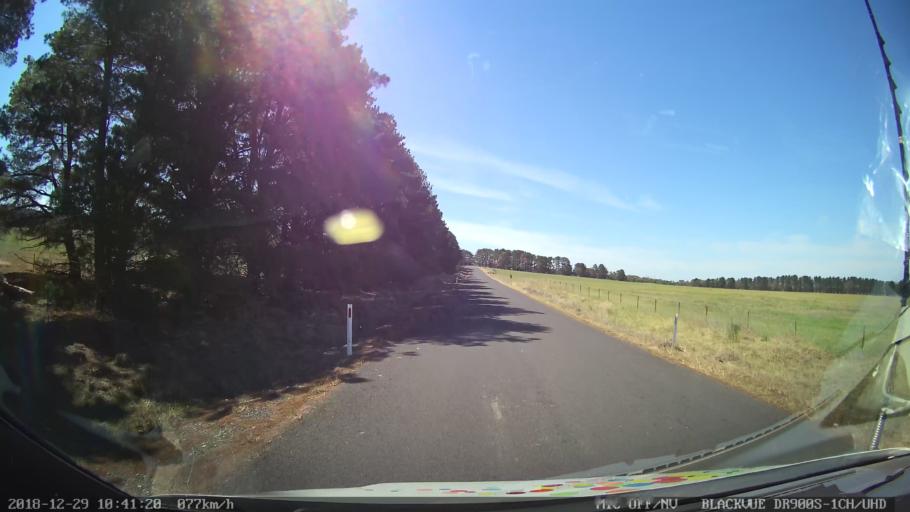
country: AU
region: New South Wales
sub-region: Palerang
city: Bungendore
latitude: -35.0242
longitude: 149.5210
